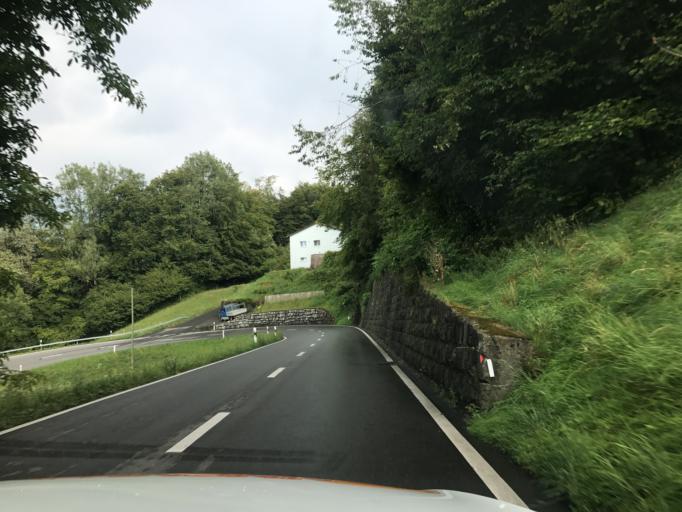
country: CH
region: Bern
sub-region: Thun District
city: Thierachern
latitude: 46.7316
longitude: 7.5855
